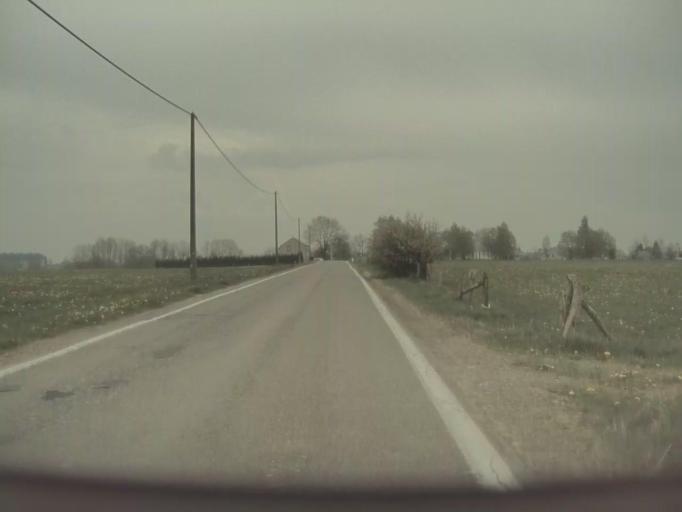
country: BE
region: Wallonia
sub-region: Province du Luxembourg
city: La Roche-en-Ardenne
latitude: 50.2155
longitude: 5.6326
